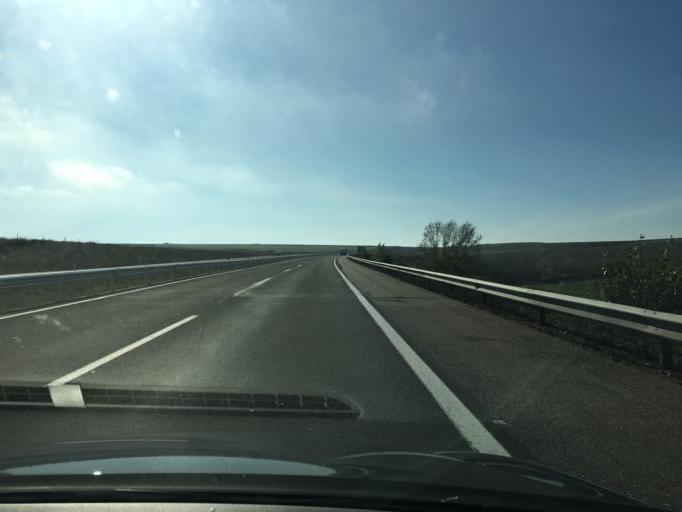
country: ES
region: Castille and Leon
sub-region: Provincia de Burgos
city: Zuneda
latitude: 42.5966
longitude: -3.2274
